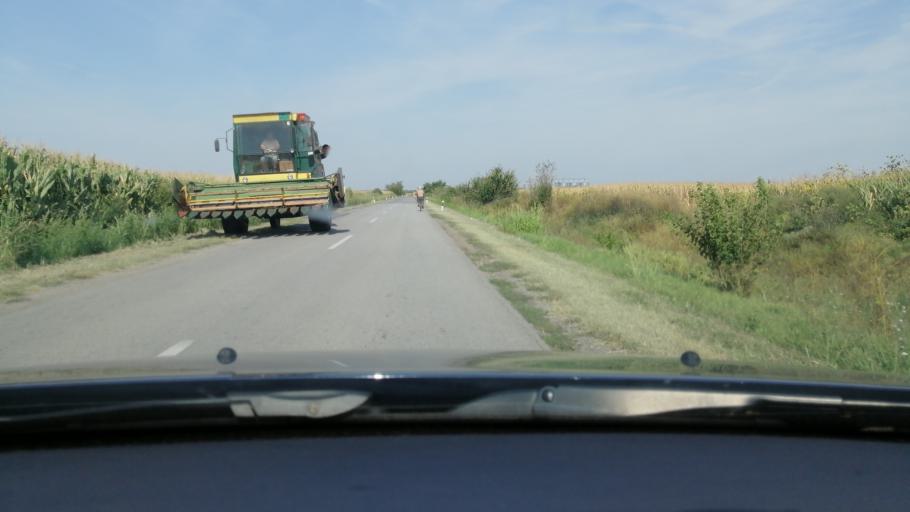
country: RS
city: Stajicevo
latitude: 45.3161
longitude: 20.4670
